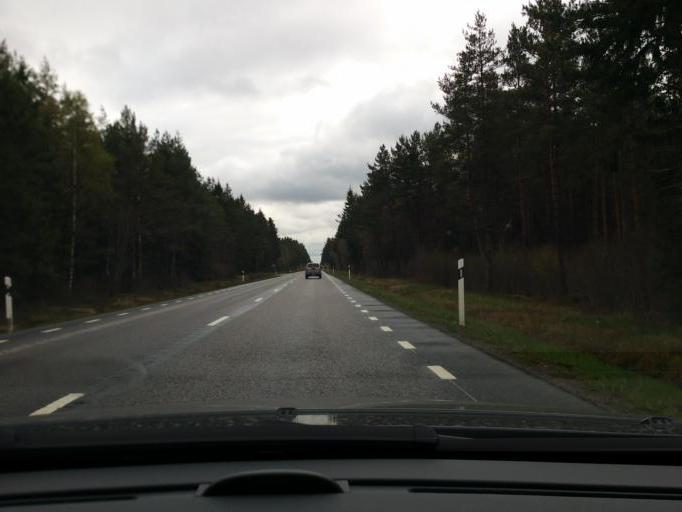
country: SE
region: Kronoberg
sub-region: Vaxjo Kommun
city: Ingelstad
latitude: 56.8036
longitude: 14.8905
